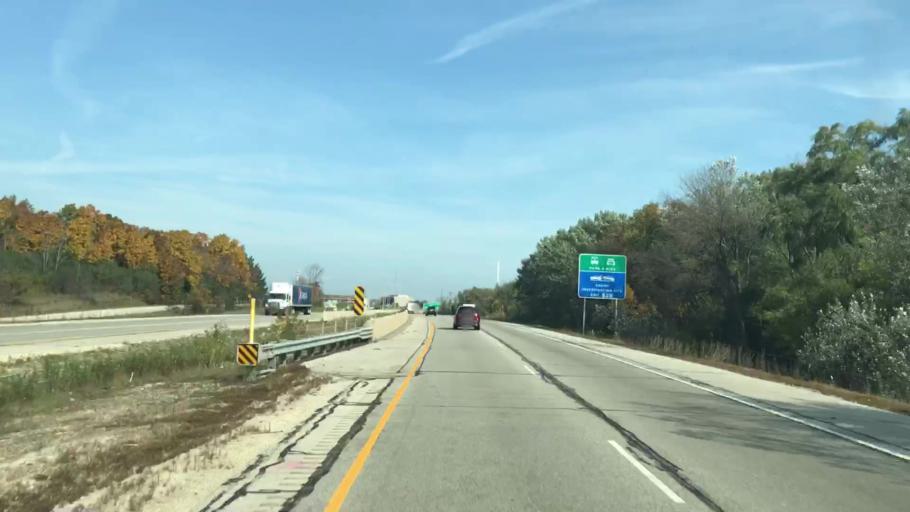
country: US
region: Wisconsin
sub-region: Milwaukee County
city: River Hills
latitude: 43.1702
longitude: -87.9156
